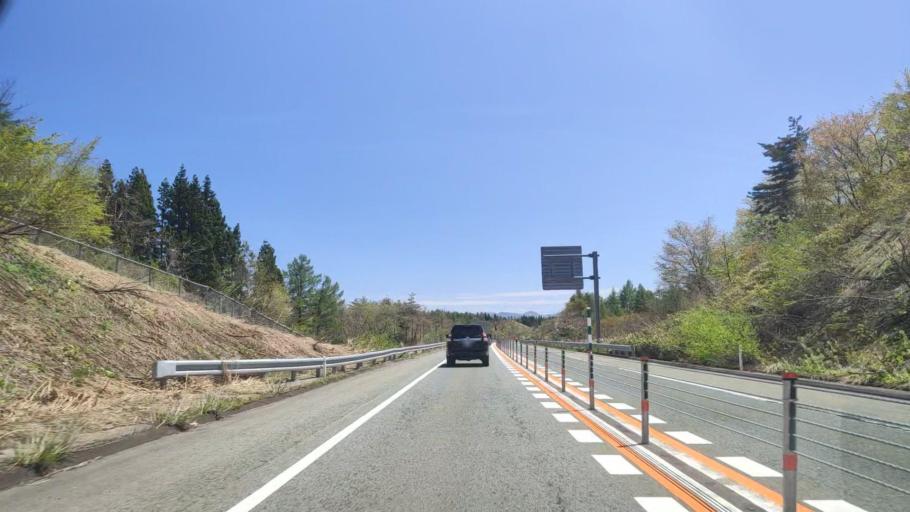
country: JP
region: Yamagata
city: Obanazawa
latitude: 38.6517
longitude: 140.3698
